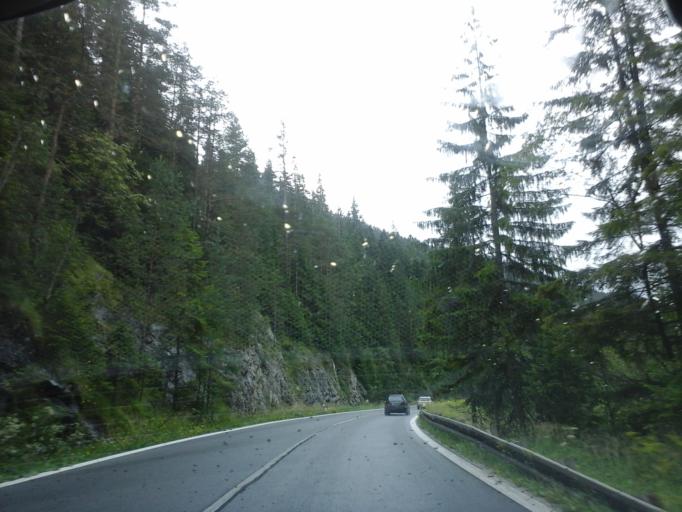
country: SK
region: Kosicky
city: Dobsina
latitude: 48.8793
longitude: 20.3121
